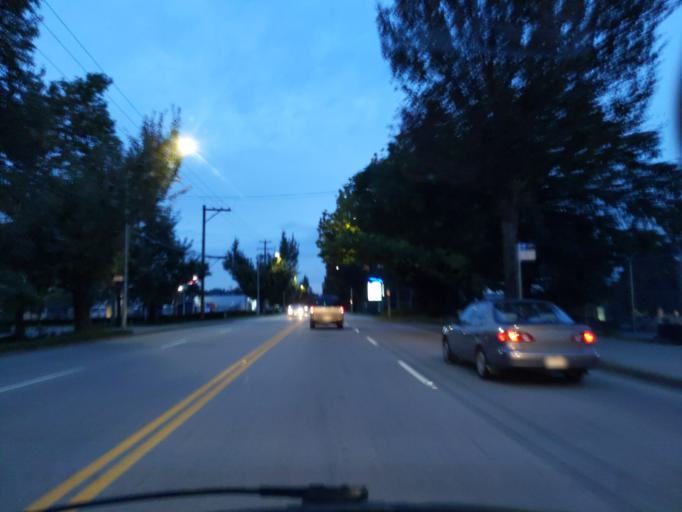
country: CA
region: British Columbia
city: Walnut Grove
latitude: 49.1770
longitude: -122.6814
